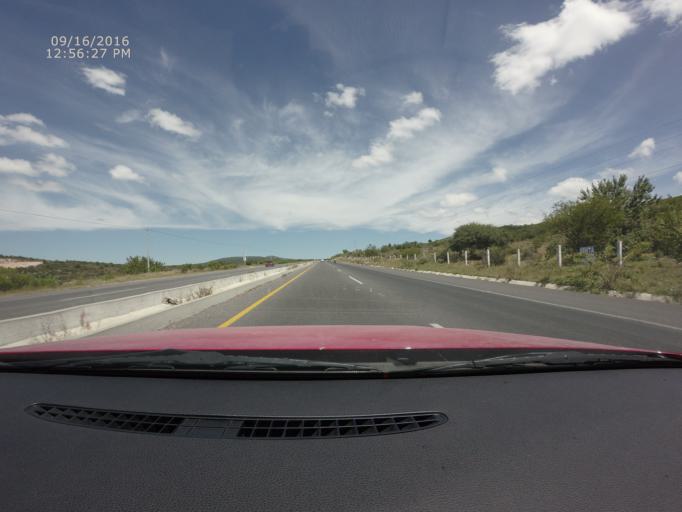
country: MX
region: Queretaro
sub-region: Colon
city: Purisima de Cubos (La Purisima)
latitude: 20.6541
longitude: -100.0993
